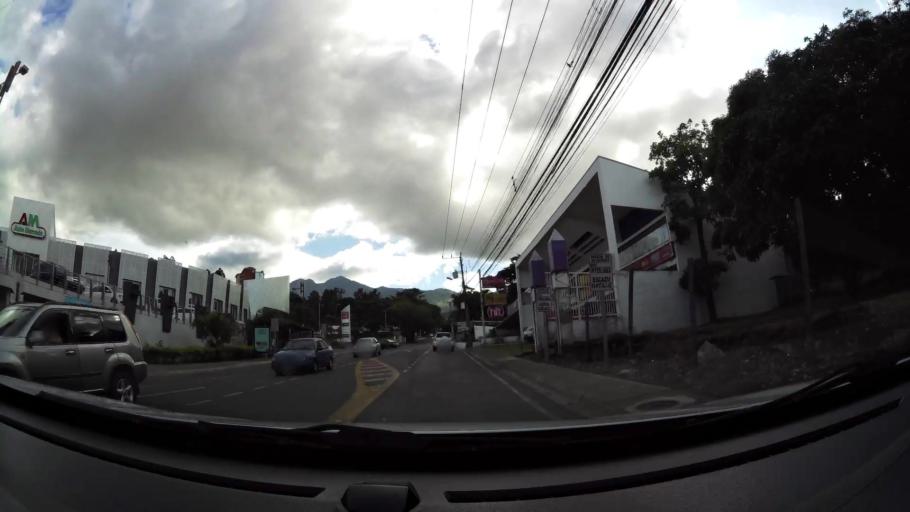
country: CR
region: San Jose
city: San Rafael
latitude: 9.9278
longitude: -84.1341
